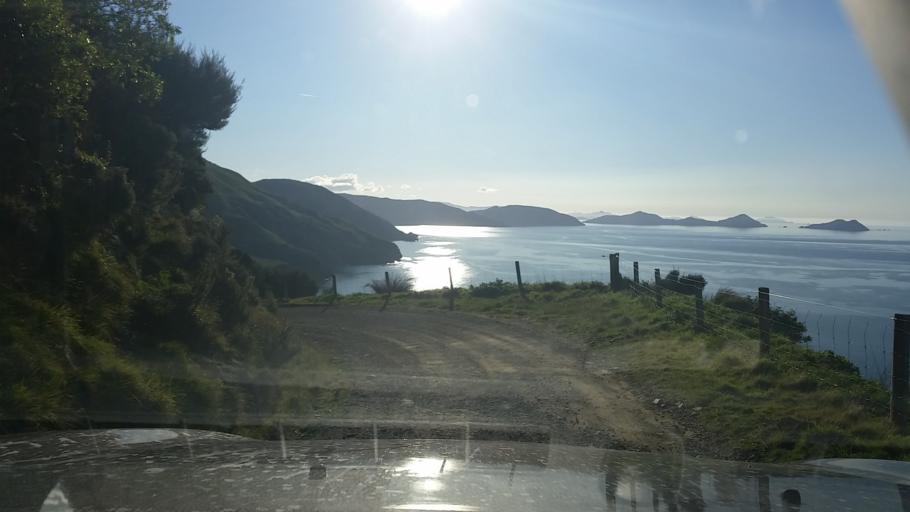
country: NZ
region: Marlborough
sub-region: Marlborough District
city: Picton
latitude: -41.0242
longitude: 174.1465
